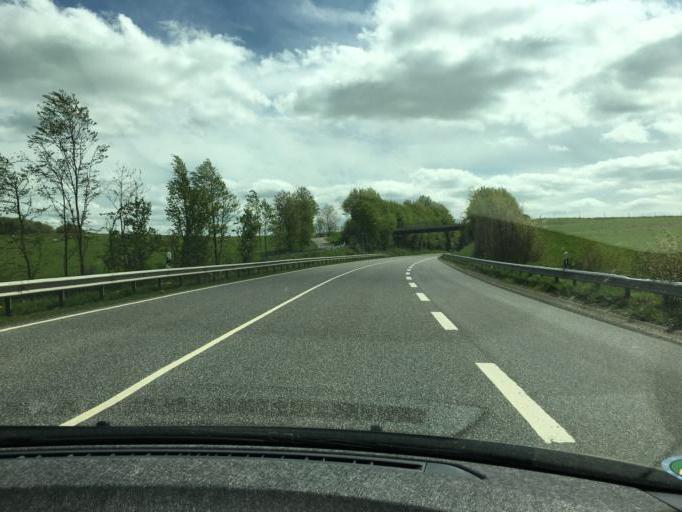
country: DE
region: Rheinland-Pfalz
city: Kempenich
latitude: 50.4229
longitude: 7.1261
